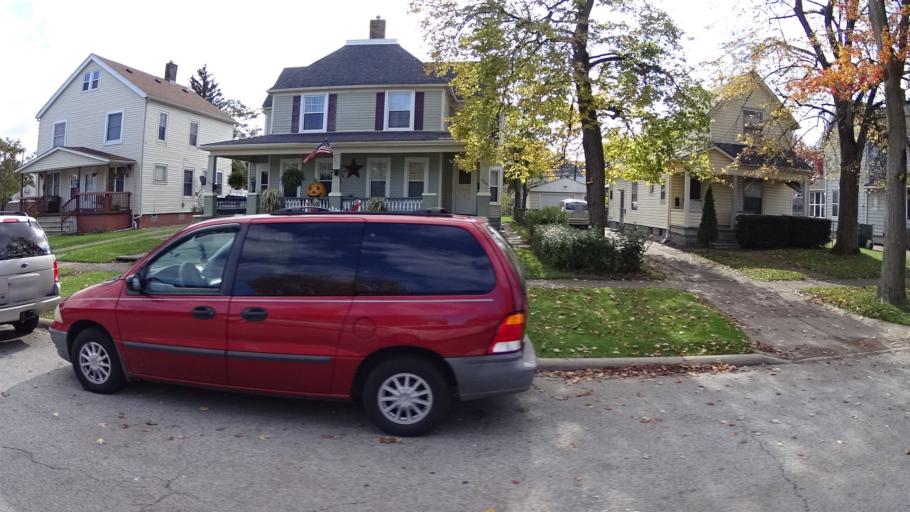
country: US
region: Ohio
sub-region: Lorain County
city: Sheffield
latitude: 41.4445
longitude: -82.1347
